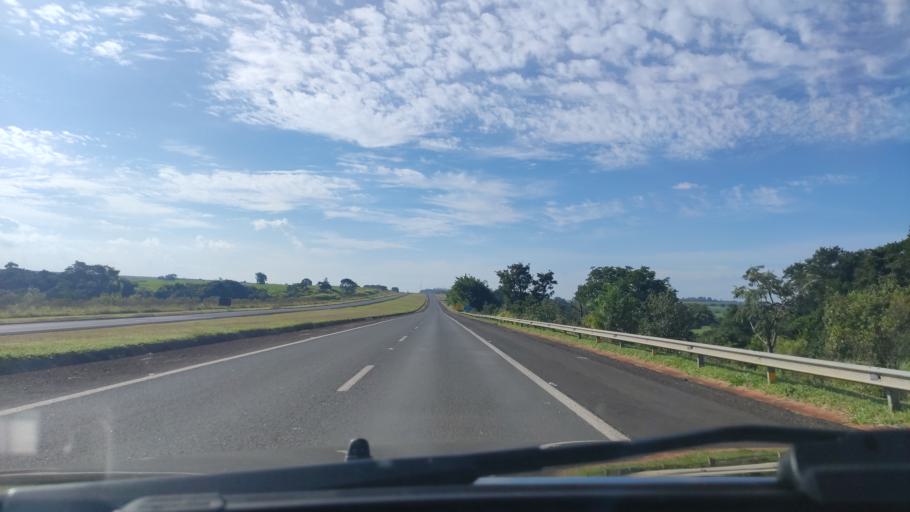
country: BR
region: Sao Paulo
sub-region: Itatinga
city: Itatinga
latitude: -22.9845
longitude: -48.7694
